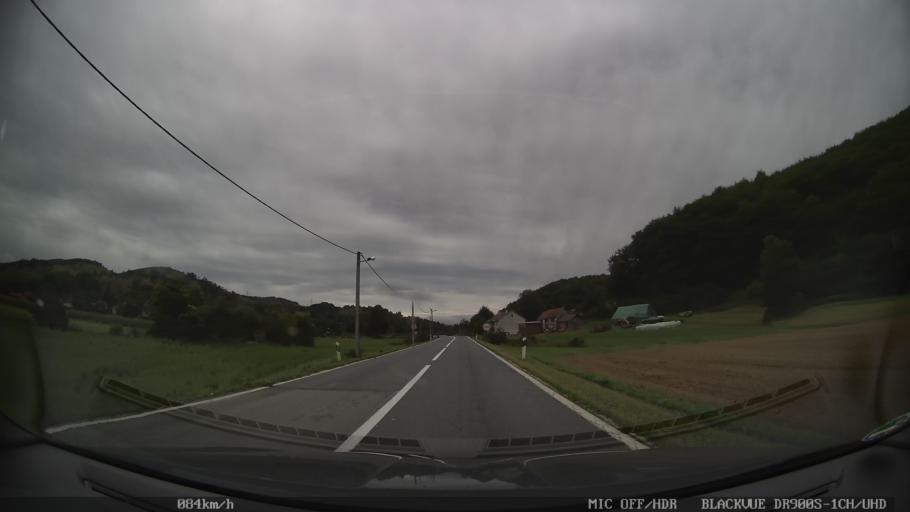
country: HR
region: Licko-Senjska
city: Brinje
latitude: 44.9336
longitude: 15.1310
